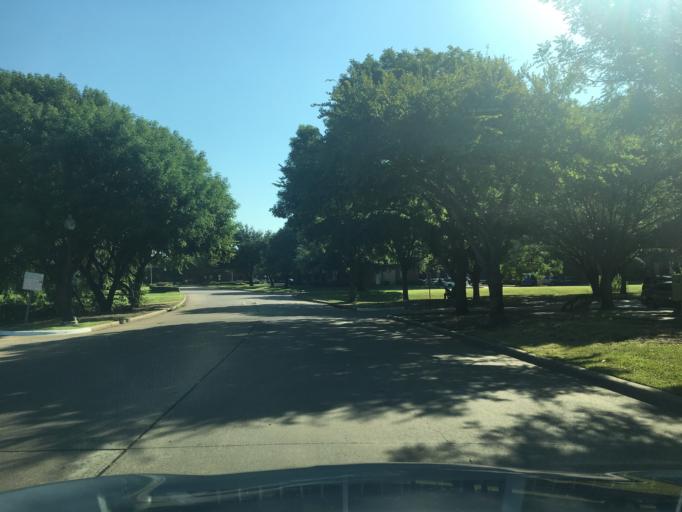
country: US
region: Texas
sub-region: Dallas County
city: Addison
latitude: 32.9608
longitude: -96.8512
